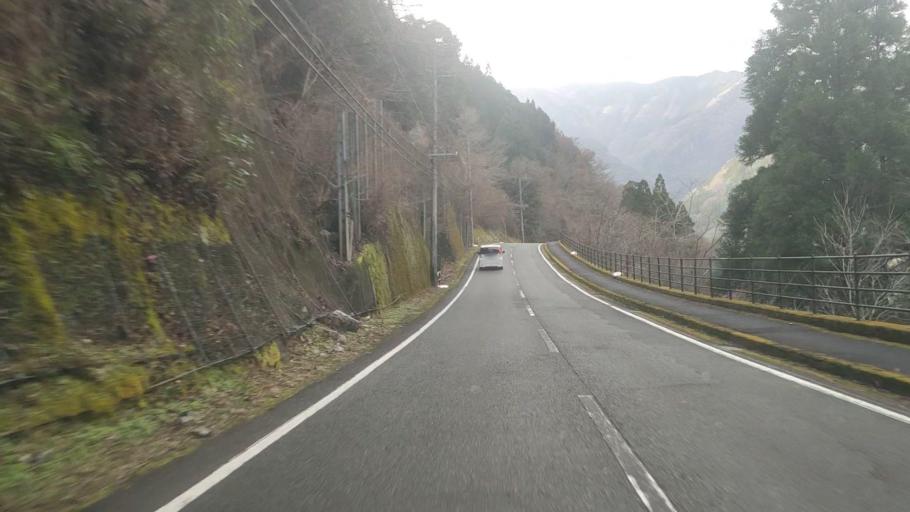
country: JP
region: Kumamoto
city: Hitoyoshi
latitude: 32.4082
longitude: 130.8292
